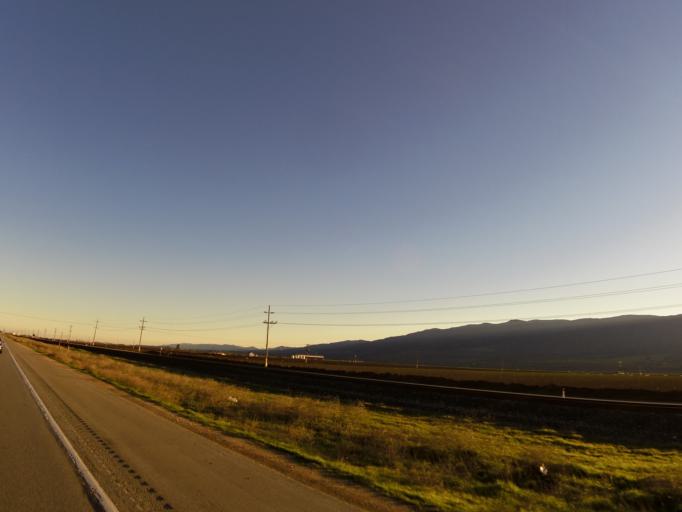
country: US
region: California
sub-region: Monterey County
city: Gonzales
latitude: 36.4818
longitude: -121.4150
